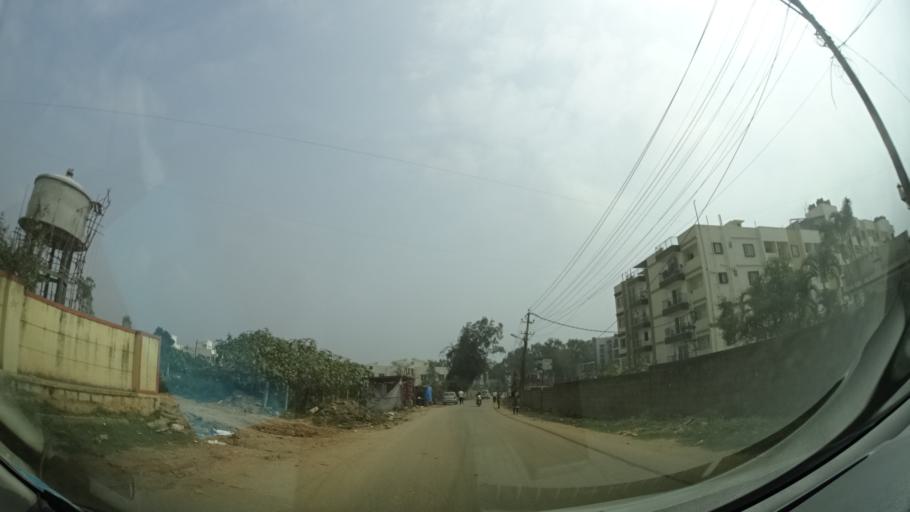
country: IN
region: Karnataka
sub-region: Bangalore Rural
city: Hoskote
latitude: 12.9767
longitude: 77.7577
